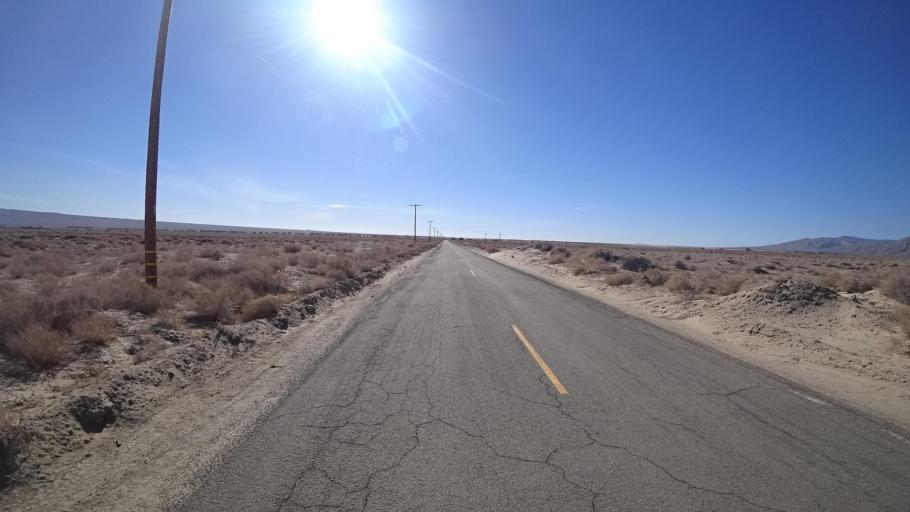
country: US
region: California
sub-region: Kern County
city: California City
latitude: 35.3014
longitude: -117.9682
